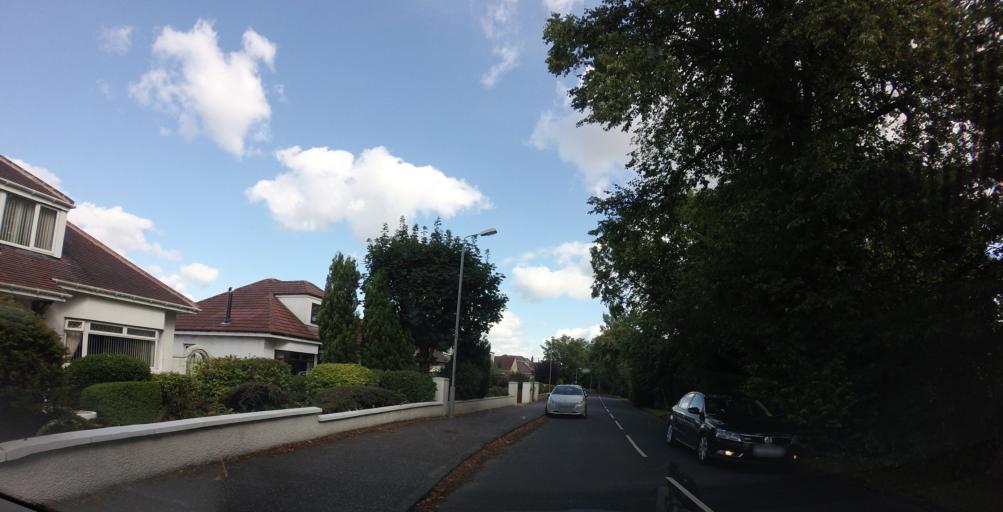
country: GB
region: Scotland
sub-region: North Lanarkshire
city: Coatbridge
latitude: 55.8601
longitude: -4.0485
